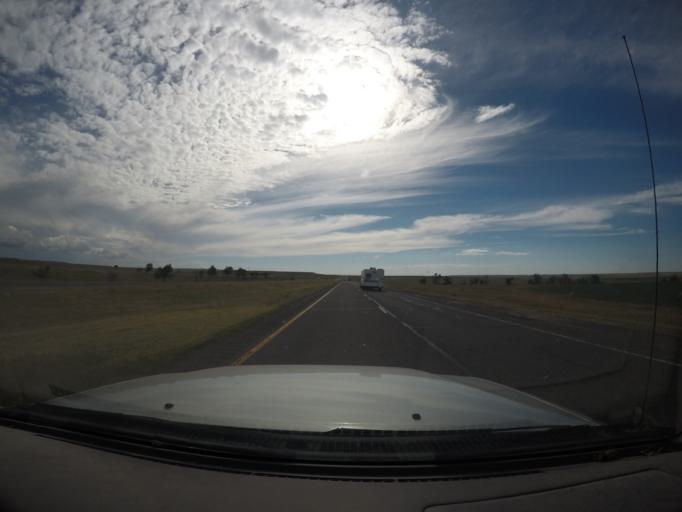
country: US
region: Wyoming
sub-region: Laramie County
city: Pine Bluffs
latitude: 41.1922
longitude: -103.9463
